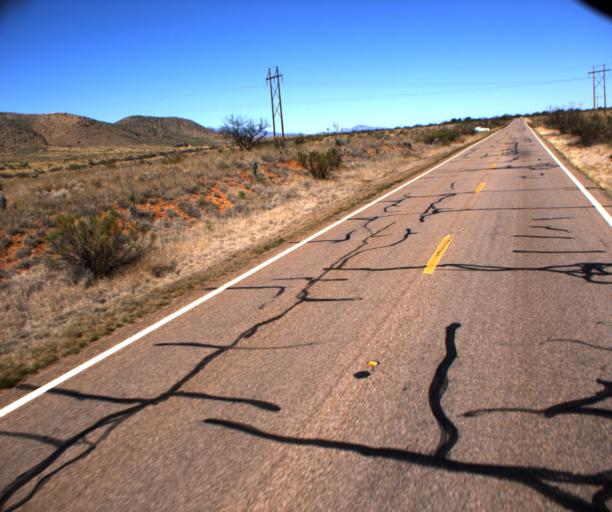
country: US
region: Arizona
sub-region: Cochise County
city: Huachuca City
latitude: 31.7206
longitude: -110.4785
